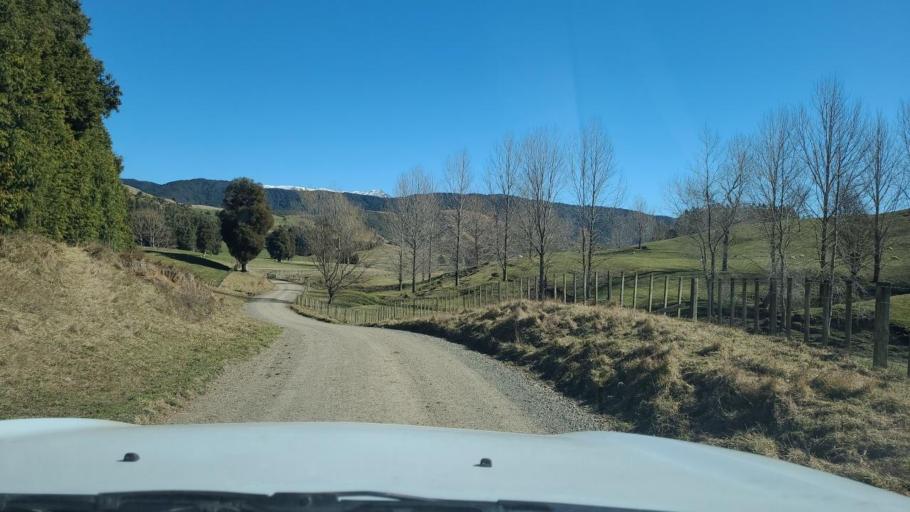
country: NZ
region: Hawke's Bay
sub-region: Napier City
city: Taradale
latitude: -39.2842
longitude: 176.4936
